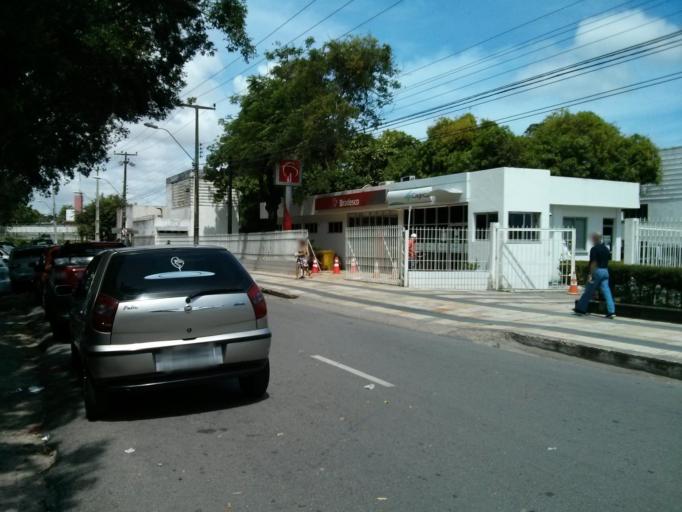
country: BR
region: Ceara
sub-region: Fortaleza
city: Fortaleza
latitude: -3.7719
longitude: -38.5353
